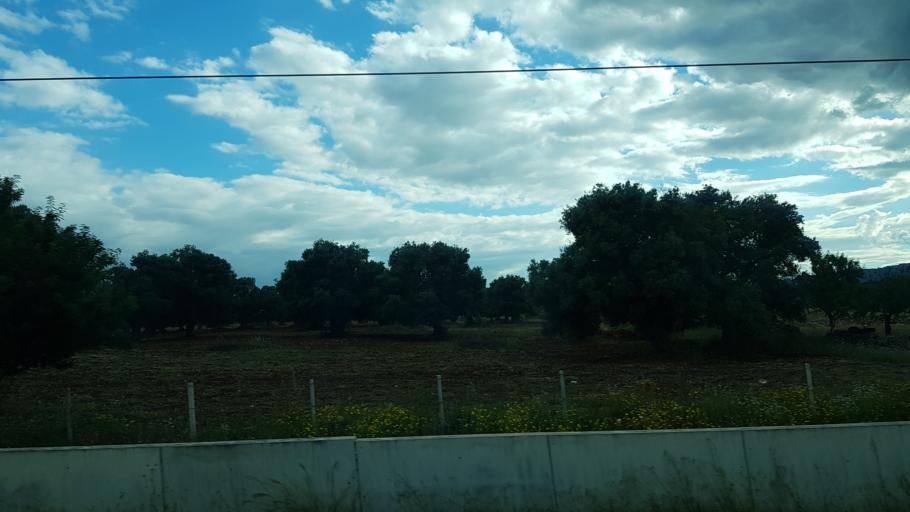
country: IT
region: Apulia
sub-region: Provincia di Brindisi
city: Pezze di Greco
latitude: 40.8436
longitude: 17.3983
